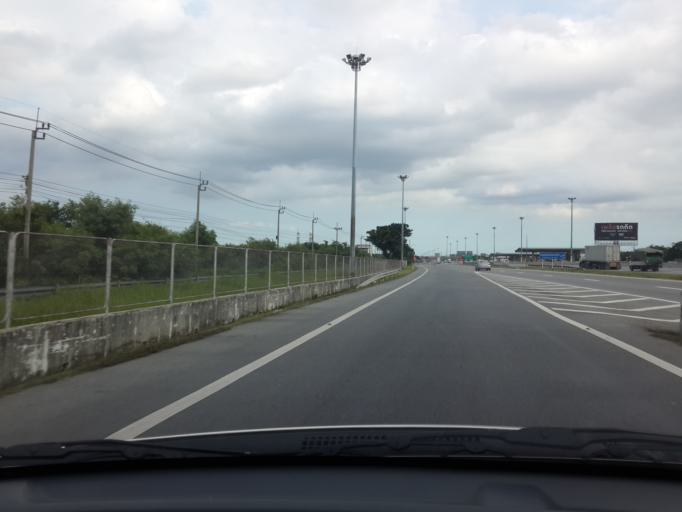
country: TH
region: Bangkok
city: Saphan Sung
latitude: 13.7775
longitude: 100.6879
